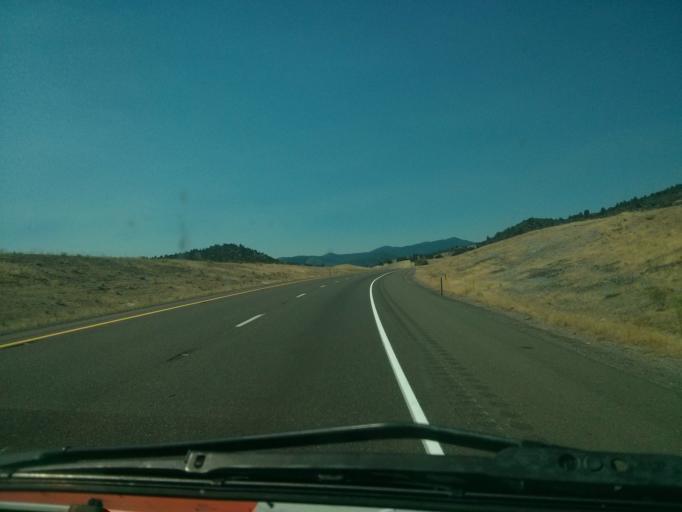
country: US
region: California
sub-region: Siskiyou County
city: Yreka
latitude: 41.7616
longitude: -122.5913
